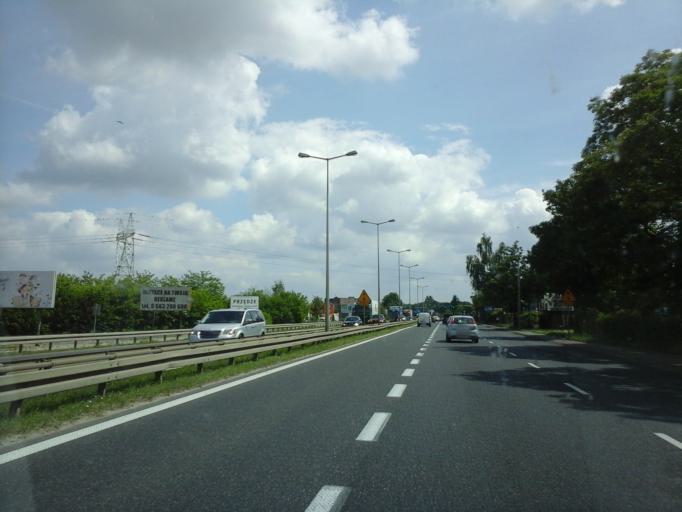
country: PL
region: Lodz Voivodeship
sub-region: Powiat lodzki wschodni
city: Tuszyn
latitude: 51.6083
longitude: 19.5311
